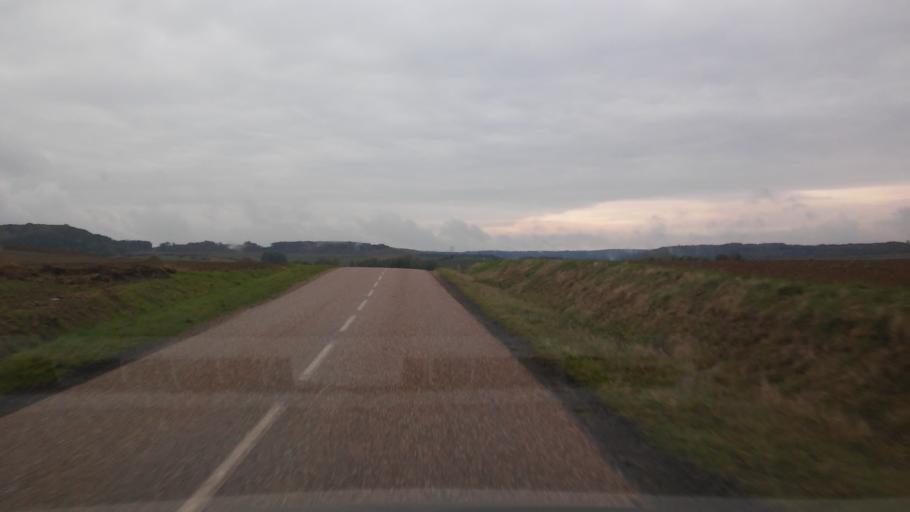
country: FR
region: Lorraine
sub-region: Departement de la Moselle
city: Boulay-Moselle
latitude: 49.1918
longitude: 6.4318
